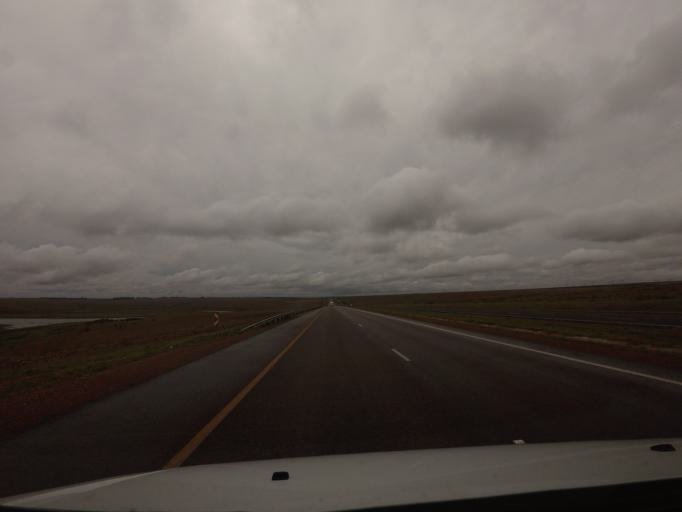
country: ZA
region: Mpumalanga
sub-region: Nkangala District Municipality
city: Middelburg
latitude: -25.8221
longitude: 29.5709
